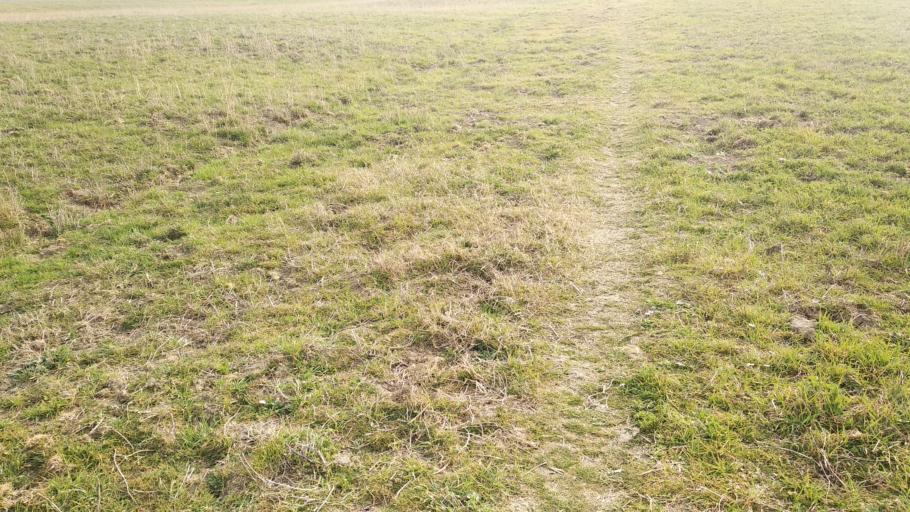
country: IT
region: Emilia-Romagna
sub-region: Provincia di Bologna
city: Ponticella
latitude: 44.4347
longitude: 11.3817
